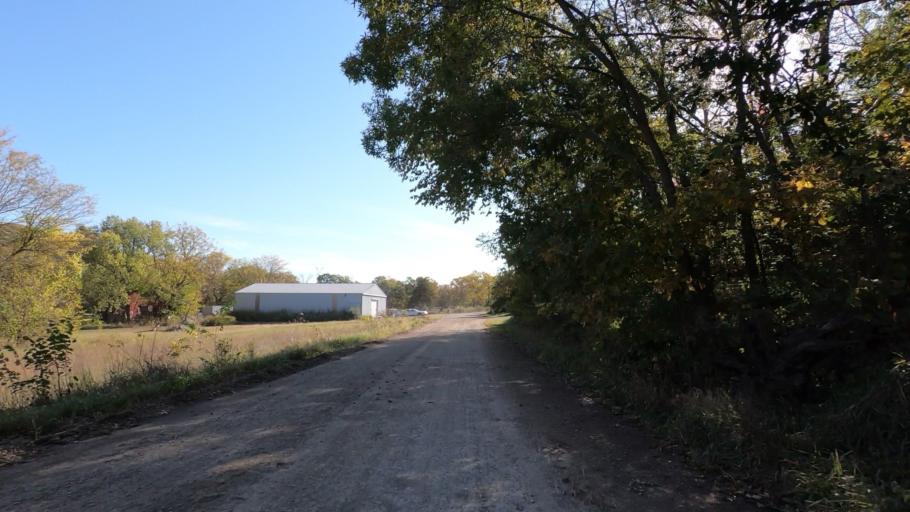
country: US
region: Kansas
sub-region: Marshall County
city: Blue Rapids
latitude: 39.4890
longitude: -96.6062
